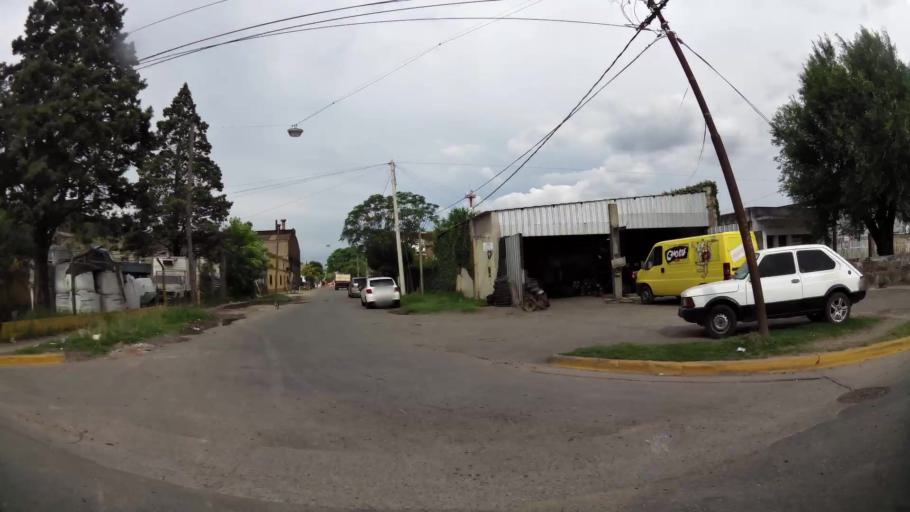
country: AR
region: Santa Fe
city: Gobernador Galvez
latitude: -33.0049
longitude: -60.6763
